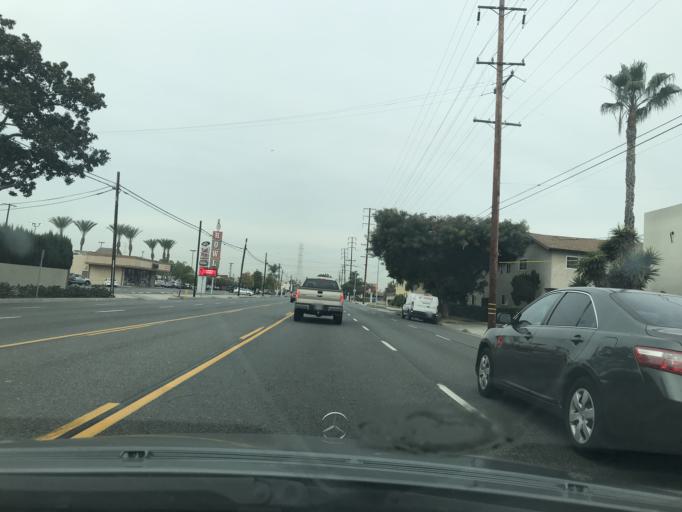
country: US
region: California
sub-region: Los Angeles County
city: Bell Gardens
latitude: 33.9576
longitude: -118.1379
